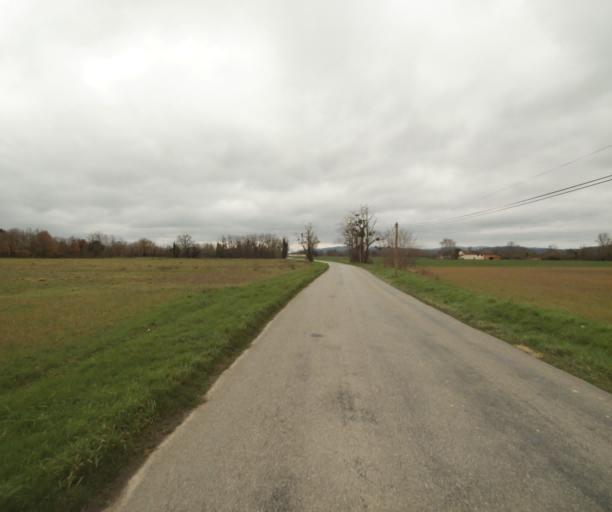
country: FR
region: Midi-Pyrenees
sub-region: Departement de l'Ariege
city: La Tour-du-Crieu
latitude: 43.1473
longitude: 1.6347
